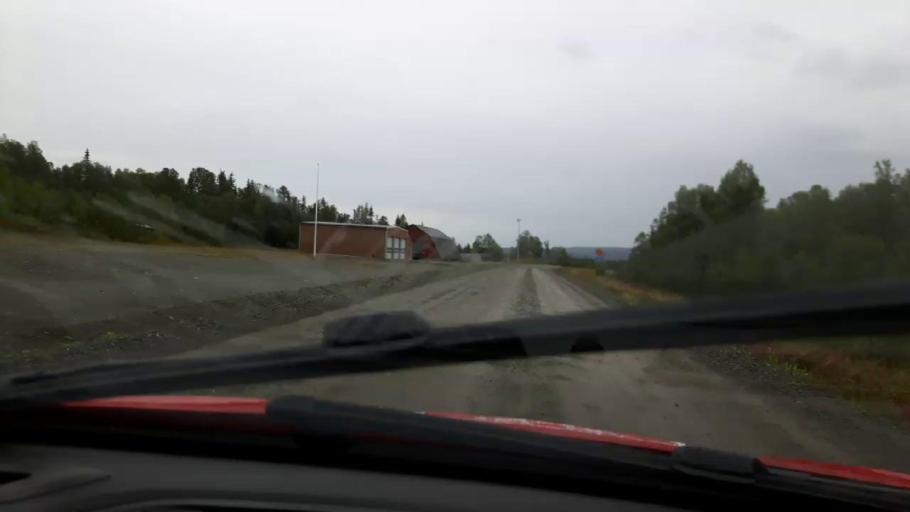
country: NO
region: Nord-Trondelag
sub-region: Meraker
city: Meraker
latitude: 63.5695
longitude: 12.2844
